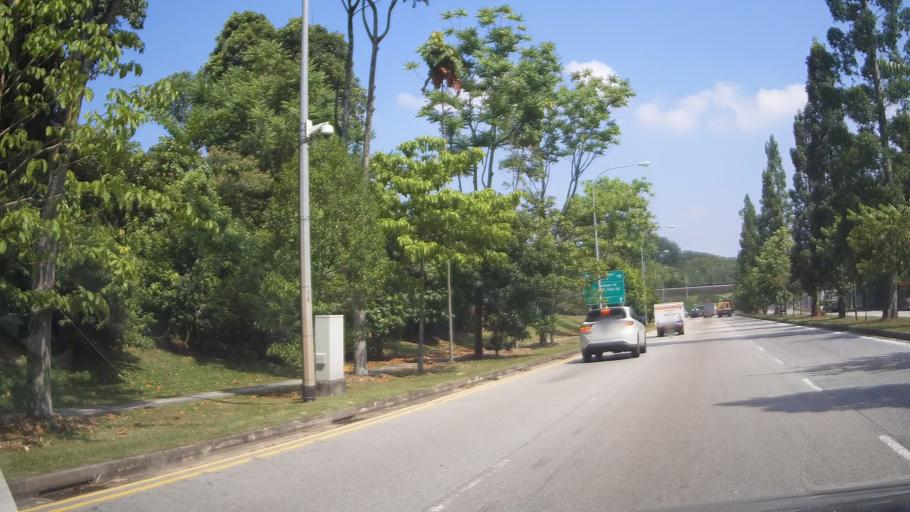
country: MY
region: Johor
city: Johor Bahru
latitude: 1.4211
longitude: 103.7581
